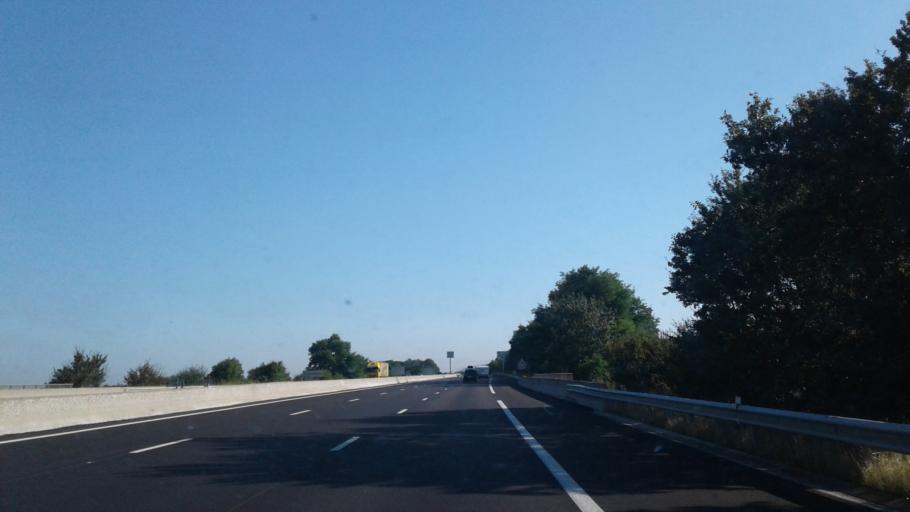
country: FR
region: Rhone-Alpes
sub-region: Departement de l'Ain
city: Certines
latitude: 46.1323
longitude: 5.2843
